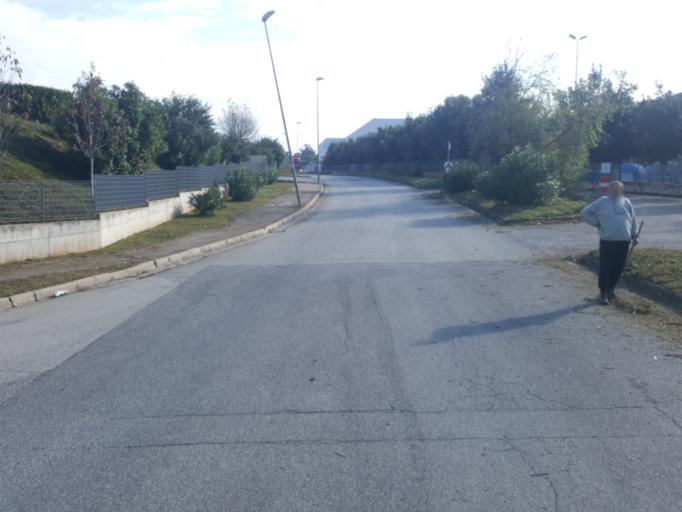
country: IT
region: Latium
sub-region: Citta metropolitana di Roma Capitale
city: Colleferro
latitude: 41.7559
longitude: 12.9945
